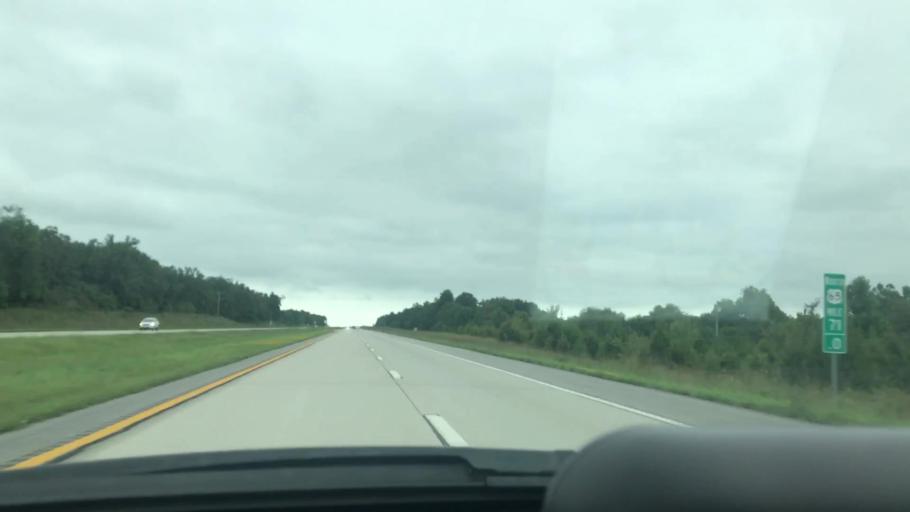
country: US
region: Missouri
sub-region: Greene County
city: Fair Grove
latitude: 37.4713
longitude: -93.1394
